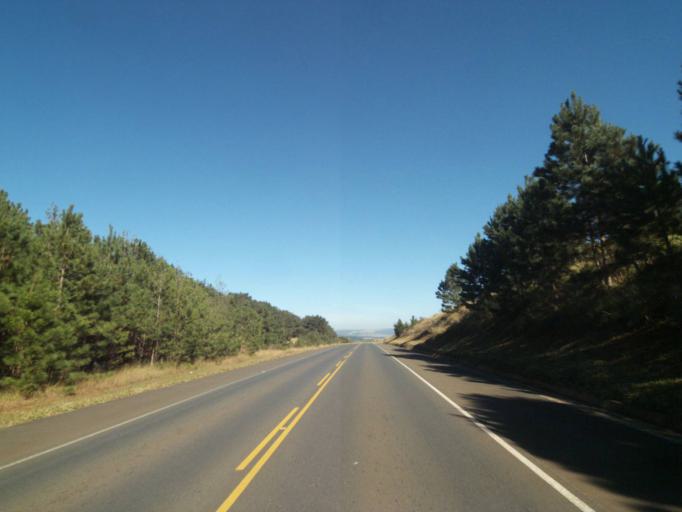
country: BR
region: Parana
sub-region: Tibagi
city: Tibagi
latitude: -24.4346
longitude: -50.4169
